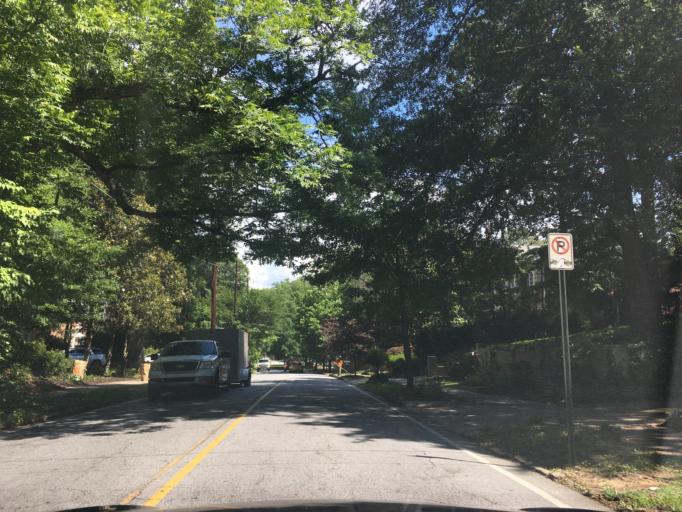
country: US
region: Georgia
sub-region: DeKalb County
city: Druid Hills
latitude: 33.8003
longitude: -84.3630
